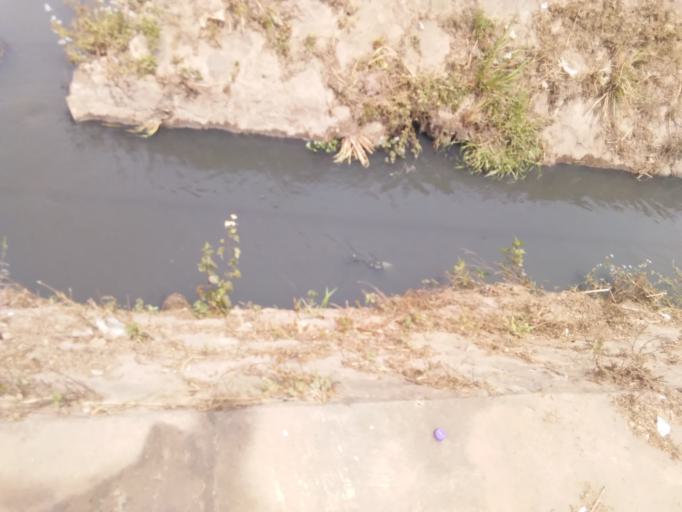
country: MX
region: Nayarit
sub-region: Tepic
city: La Corregidora
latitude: 21.4789
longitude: -104.8402
